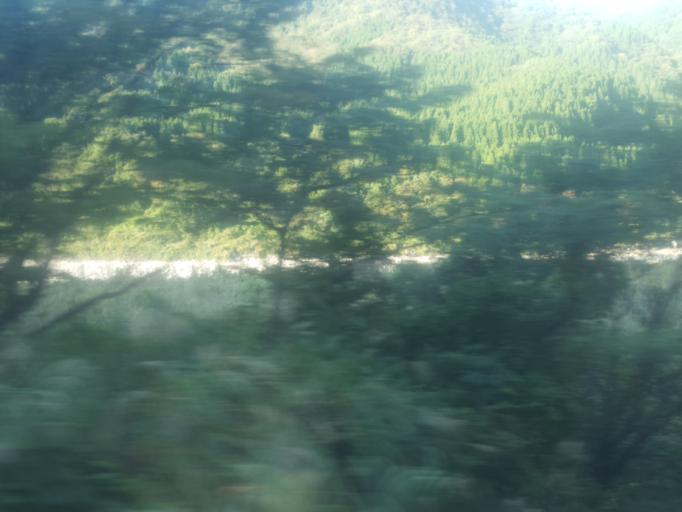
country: JP
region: Toyama
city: Kamiichi
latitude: 36.5816
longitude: 137.4252
